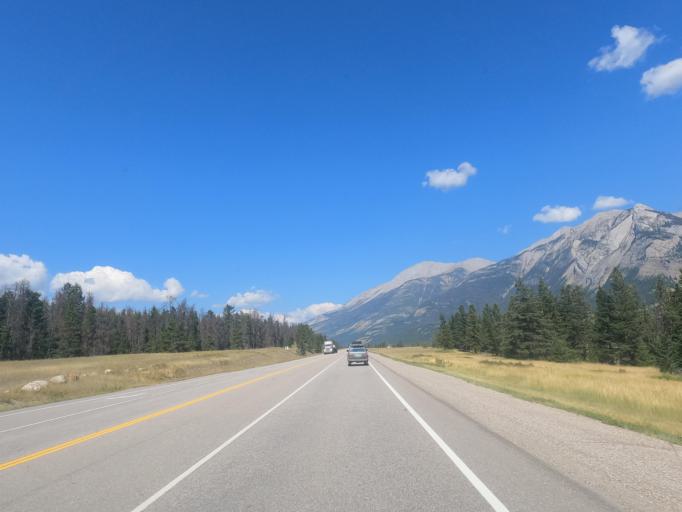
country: CA
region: Alberta
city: Jasper Park Lodge
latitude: 52.9403
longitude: -118.0394
